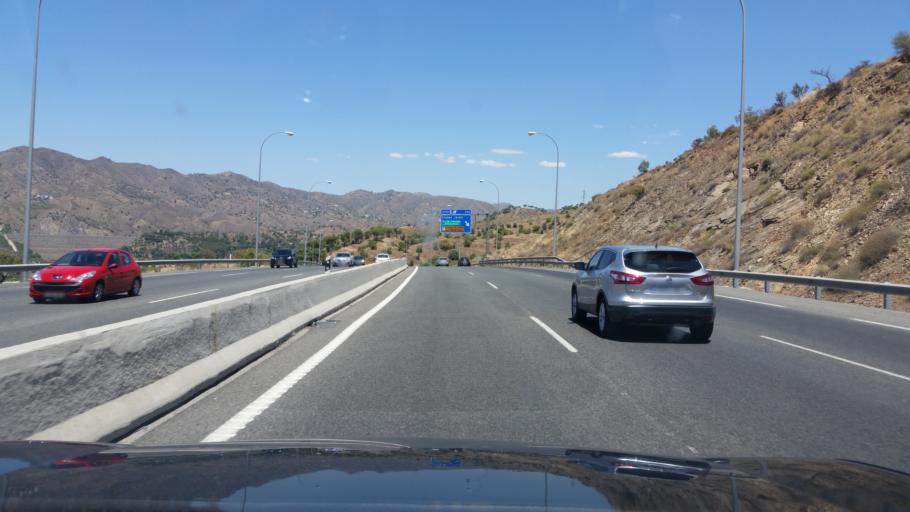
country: ES
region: Andalusia
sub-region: Provincia de Malaga
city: Malaga
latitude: 36.7469
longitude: -4.4088
